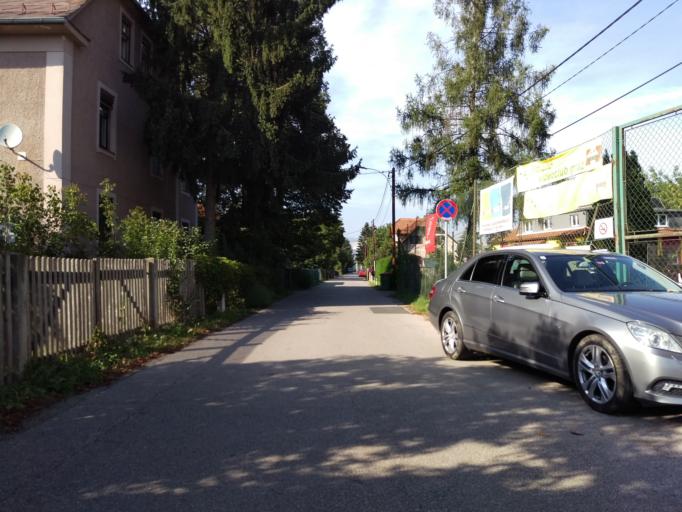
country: AT
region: Styria
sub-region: Politischer Bezirk Graz-Umgebung
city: Feldkirchen bei Graz
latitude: 47.0239
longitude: 15.4293
